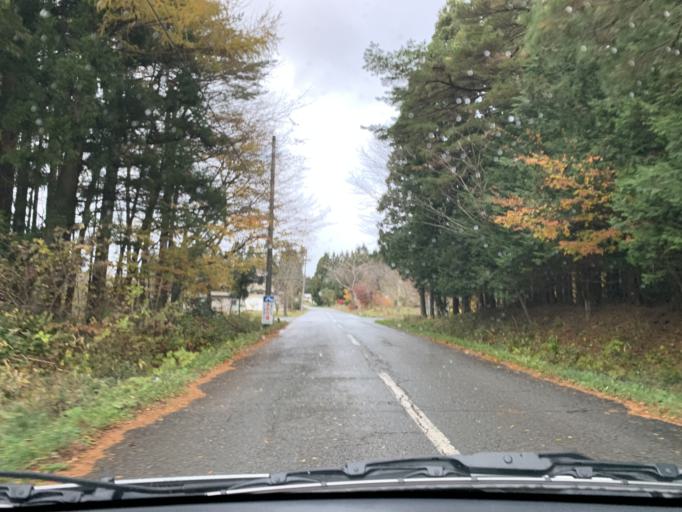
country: JP
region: Iwate
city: Mizusawa
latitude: 39.0929
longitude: 140.9934
